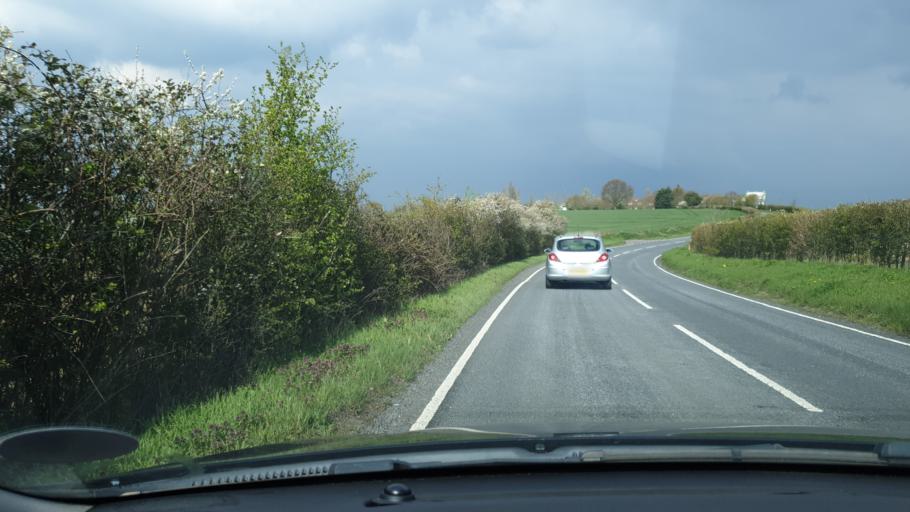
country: GB
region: England
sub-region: Essex
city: Mistley
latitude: 51.8972
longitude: 1.0918
